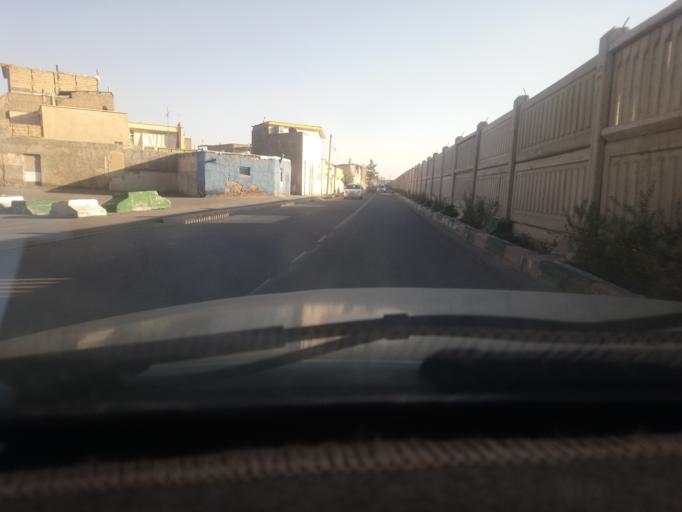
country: IR
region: Qom
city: Qom
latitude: 34.6648
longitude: 50.8676
